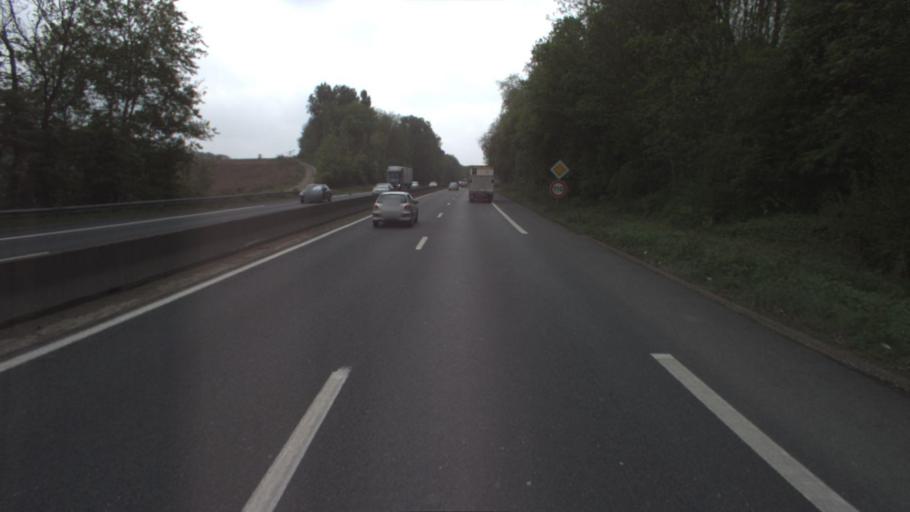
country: FR
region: Ile-de-France
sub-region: Departement de Seine-et-Marne
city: Saint-Mard
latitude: 49.0523
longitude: 2.6979
